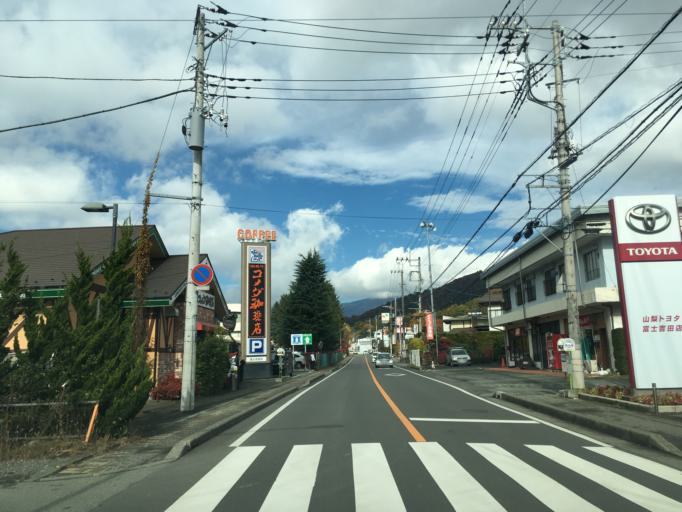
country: JP
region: Yamanashi
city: Fujikawaguchiko
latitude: 35.4876
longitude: 138.7847
